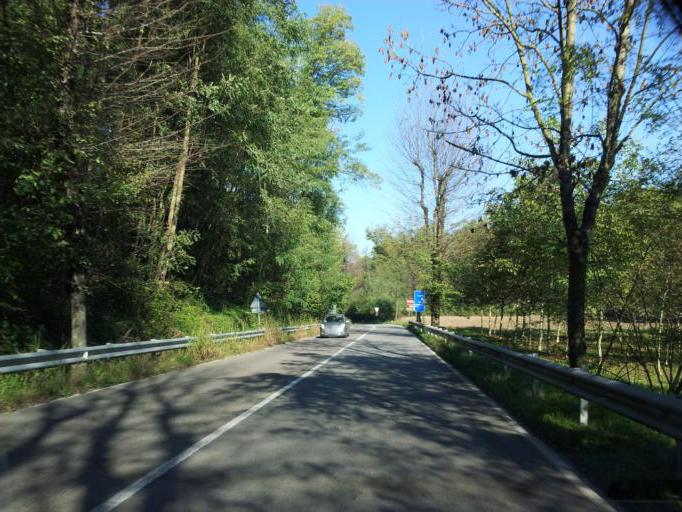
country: IT
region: Lombardy
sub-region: Provincia di Varese
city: Crosio della Valle
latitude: 45.7574
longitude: 8.7615
